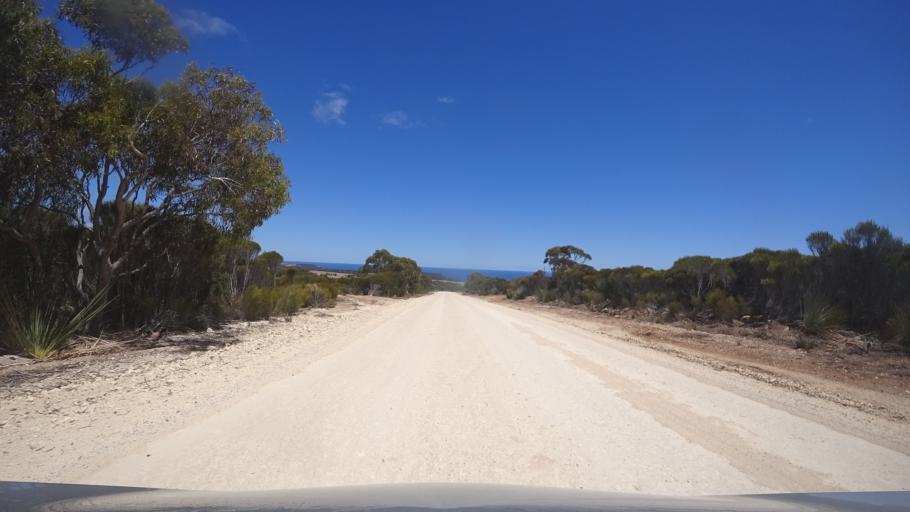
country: AU
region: South Australia
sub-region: Kangaroo Island
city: Kingscote
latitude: -35.6376
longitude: 137.2245
